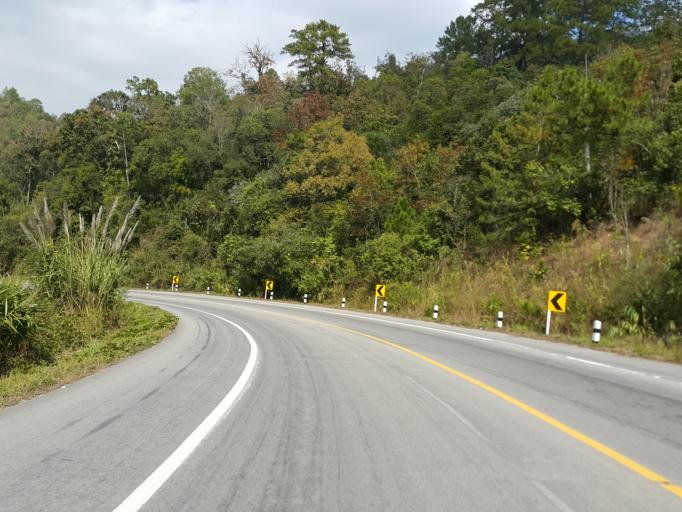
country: TH
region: Lampang
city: Wang Nuea
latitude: 19.0797
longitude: 99.4004
